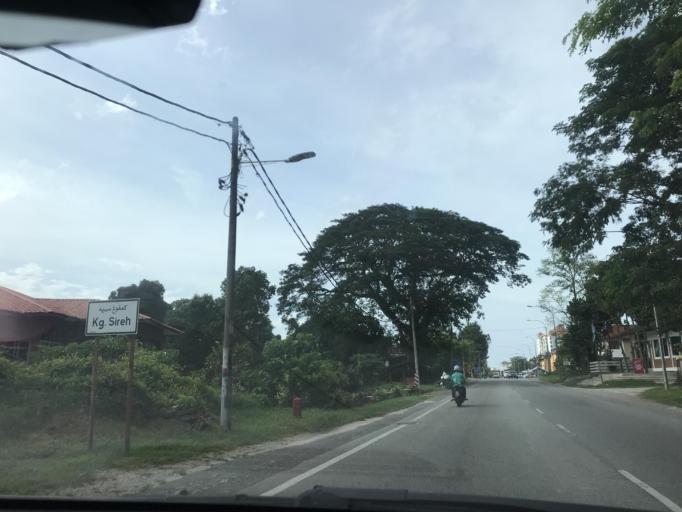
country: MY
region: Kelantan
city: Kota Bharu
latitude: 6.1060
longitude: 102.2359
